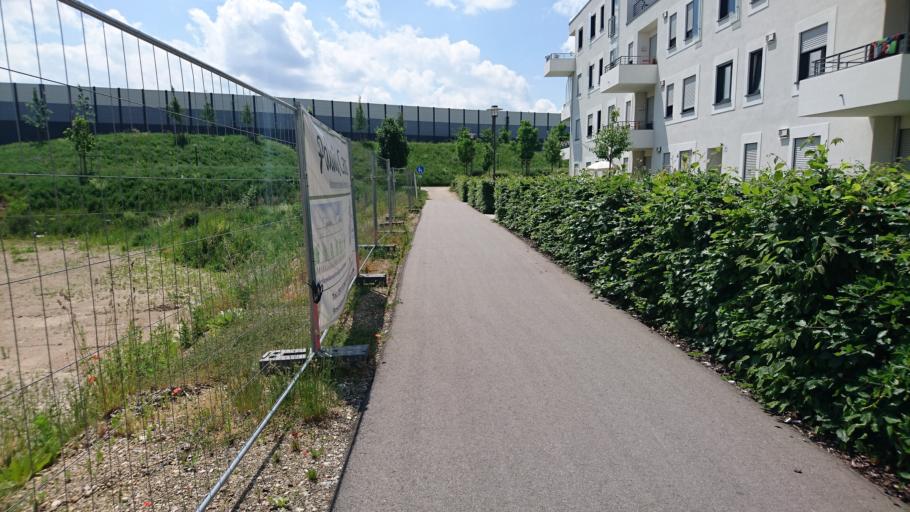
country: DE
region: Bavaria
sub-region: Upper Palatinate
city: Regensburg
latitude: 49.0128
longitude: 12.1245
